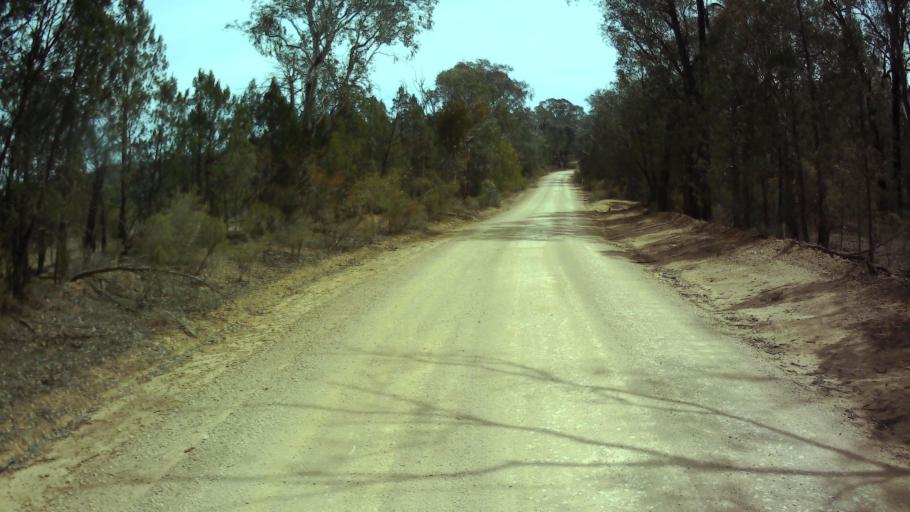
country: AU
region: New South Wales
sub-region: Weddin
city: Grenfell
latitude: -33.9159
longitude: 148.4122
